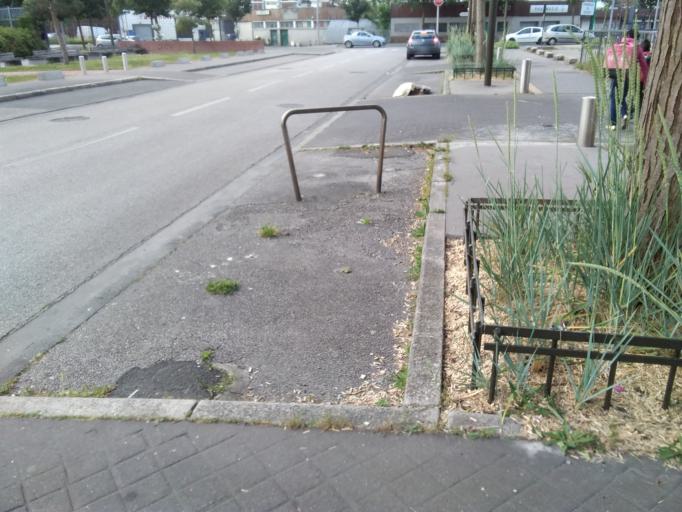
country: FR
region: Picardie
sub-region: Departement de la Somme
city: Amiens
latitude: 49.9122
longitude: 2.3078
